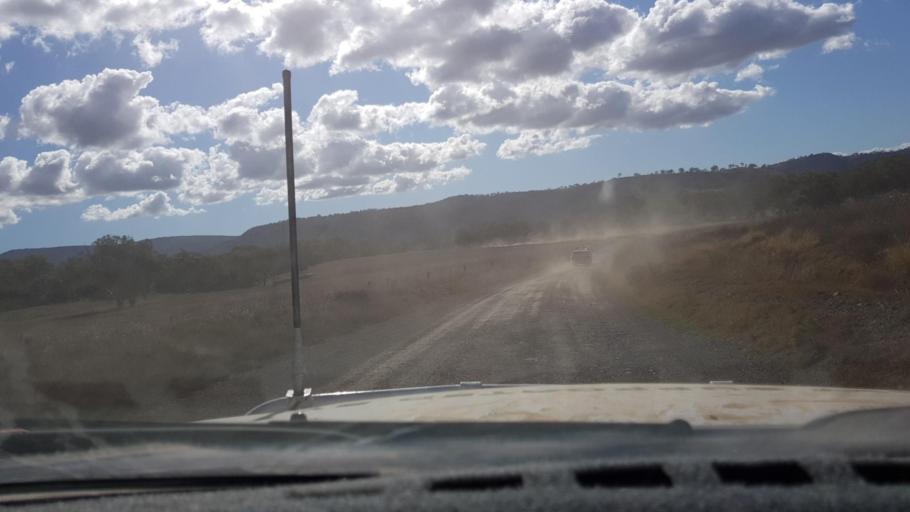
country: AU
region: New South Wales
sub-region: Tamworth Municipality
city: Manilla
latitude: -30.6236
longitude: 150.5120
